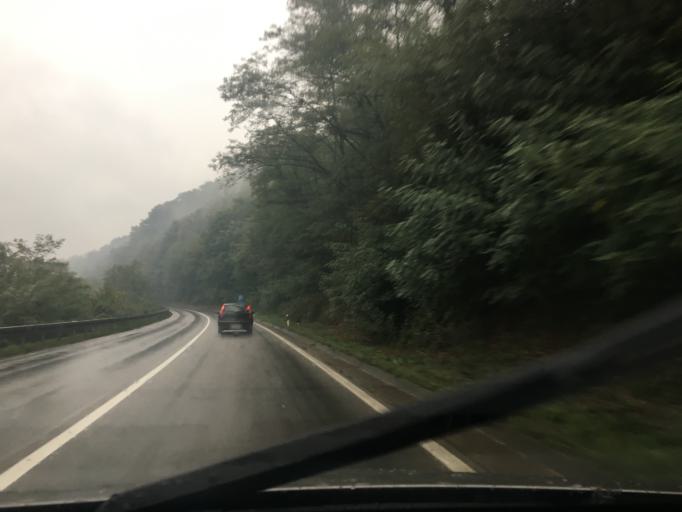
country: RS
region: Central Serbia
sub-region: Pcinjski Okrug
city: Vladicin Han
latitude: 42.7807
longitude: 22.0948
